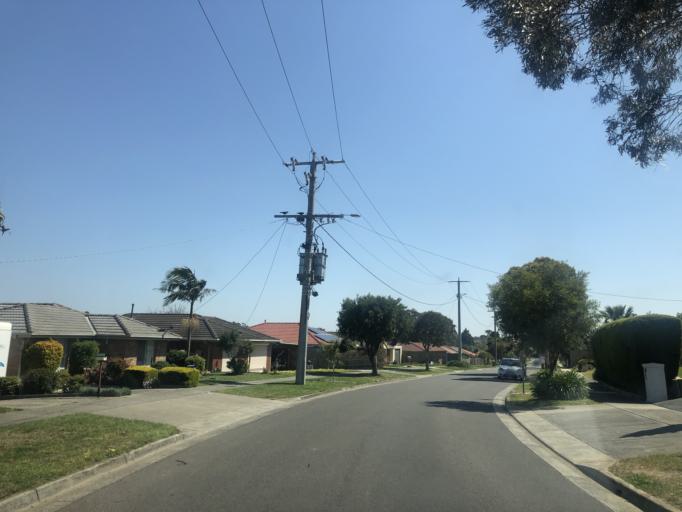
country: AU
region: Victoria
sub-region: Casey
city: Narre Warren South
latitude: -38.0353
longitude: 145.2833
